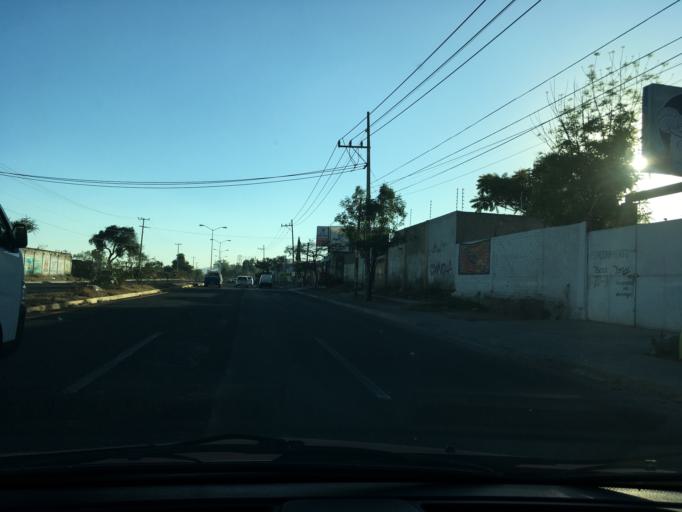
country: MX
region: Jalisco
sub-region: Tlajomulco de Zuniga
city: La Tijera
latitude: 20.5853
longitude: -103.4228
